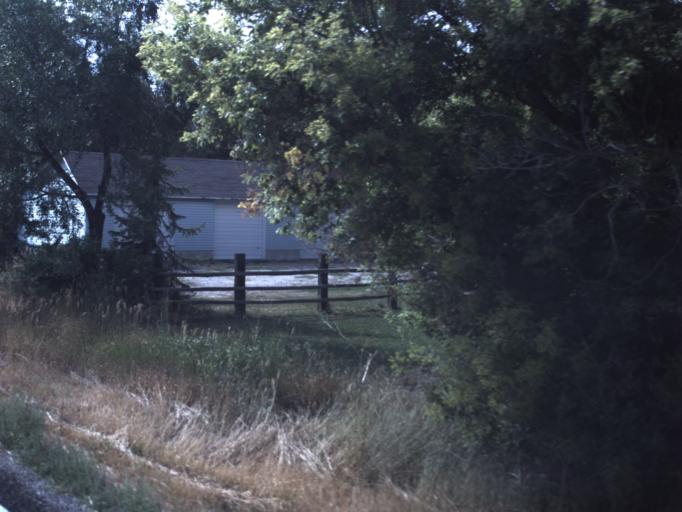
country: US
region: Utah
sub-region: Cache County
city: Benson
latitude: 41.9199
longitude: -112.0374
